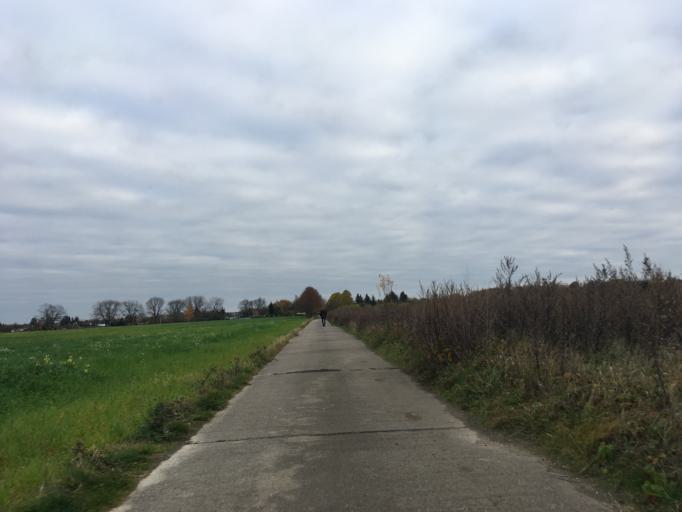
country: DE
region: Brandenburg
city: Vetschau
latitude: 51.7790
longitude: 14.0586
